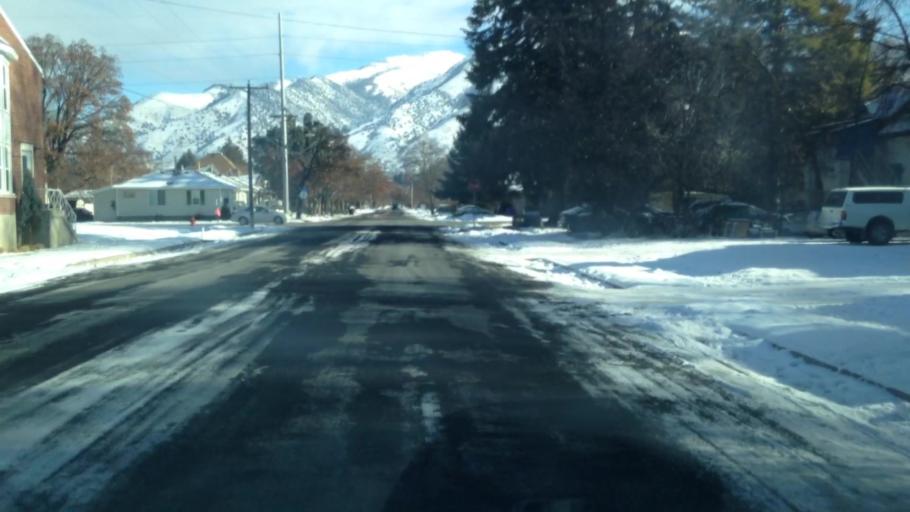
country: US
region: Utah
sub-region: Cache County
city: Logan
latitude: 41.7277
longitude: -111.8334
